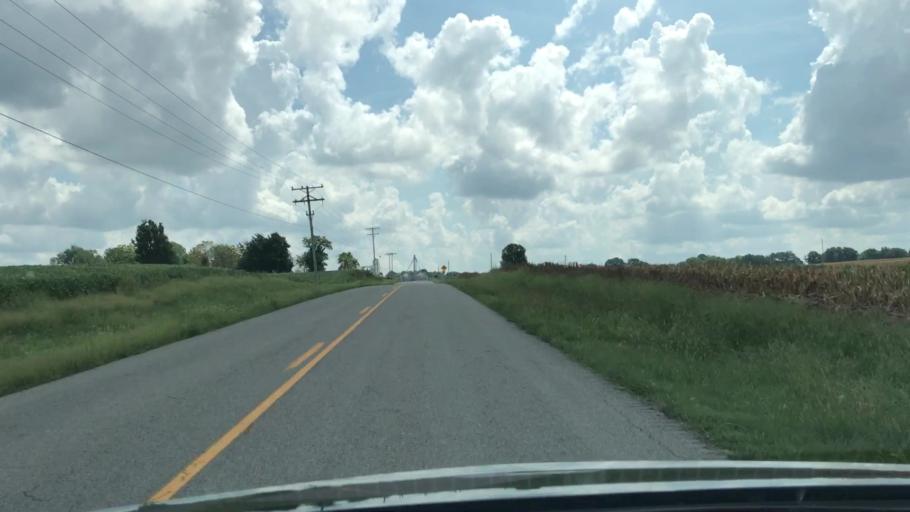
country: US
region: Kentucky
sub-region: Todd County
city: Guthrie
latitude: 36.7220
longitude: -87.0801
